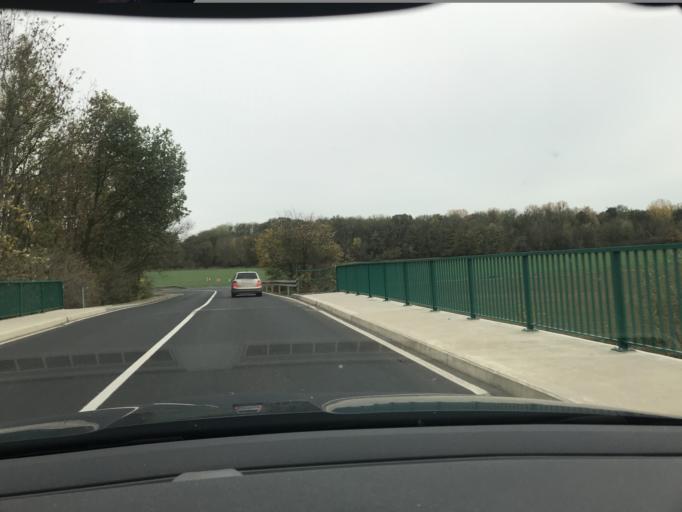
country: CZ
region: Ustecky
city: Budyne nad Ohri
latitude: 50.4097
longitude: 14.1159
